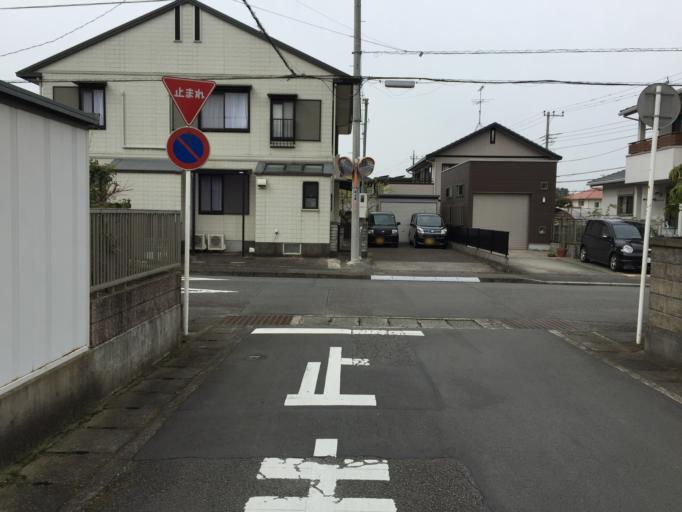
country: JP
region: Shizuoka
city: Mishima
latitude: 35.1748
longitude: 138.9253
